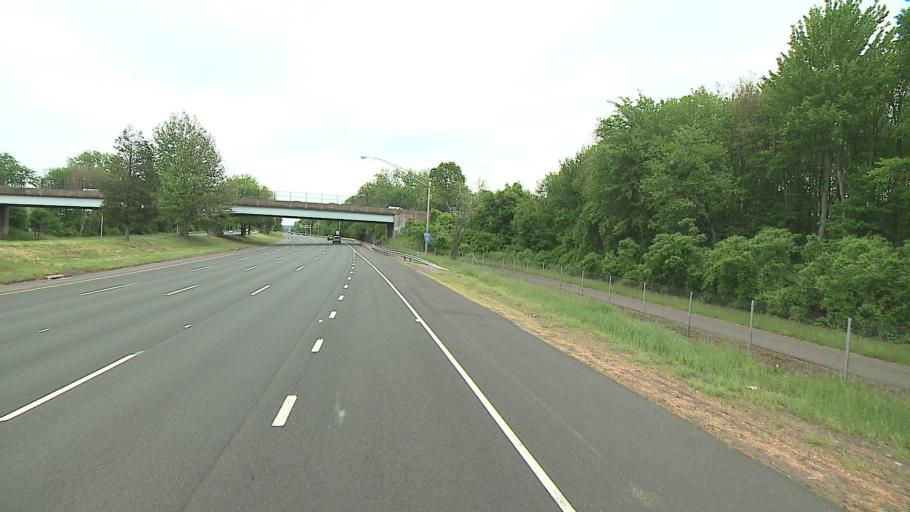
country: US
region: Connecticut
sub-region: Hartford County
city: East Hartford
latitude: 41.7645
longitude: -72.5701
